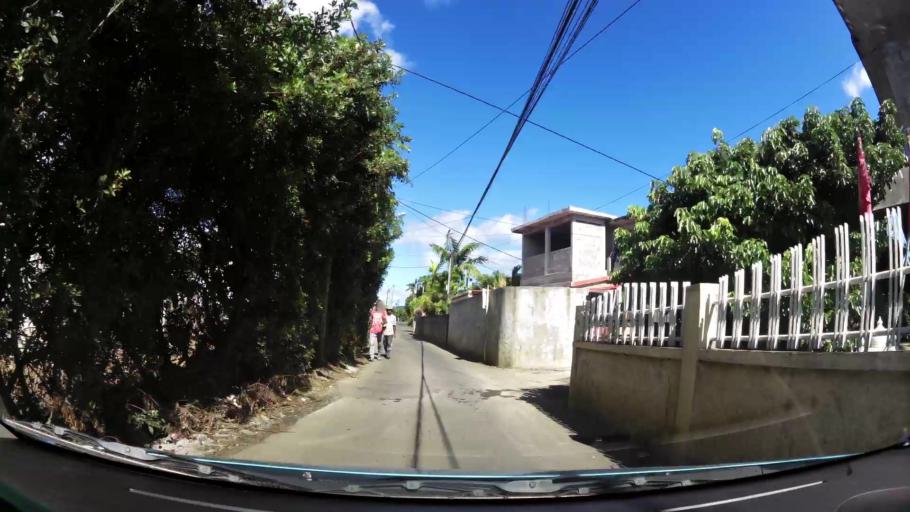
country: MU
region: Plaines Wilhems
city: Vacoas
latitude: -20.3152
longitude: 57.4912
